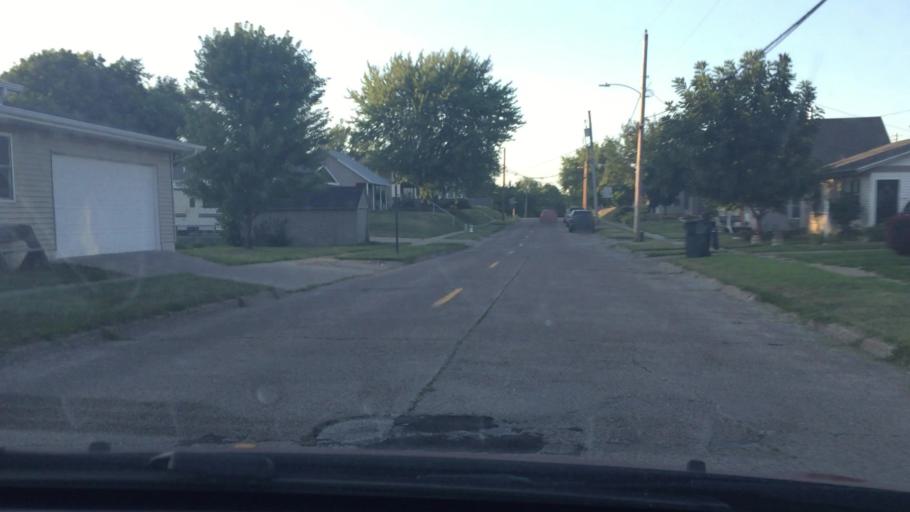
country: US
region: Iowa
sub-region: Muscatine County
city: Muscatine
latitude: 41.4208
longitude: -91.0651
